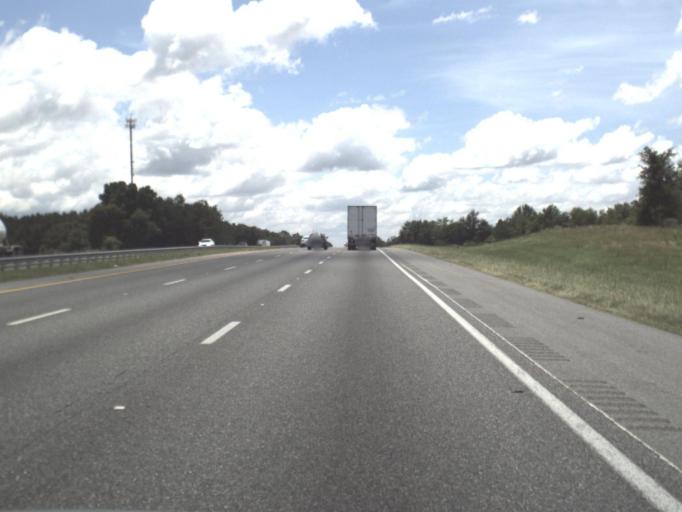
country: US
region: Florida
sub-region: Columbia County
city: Lake City
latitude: 30.0536
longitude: -82.6230
